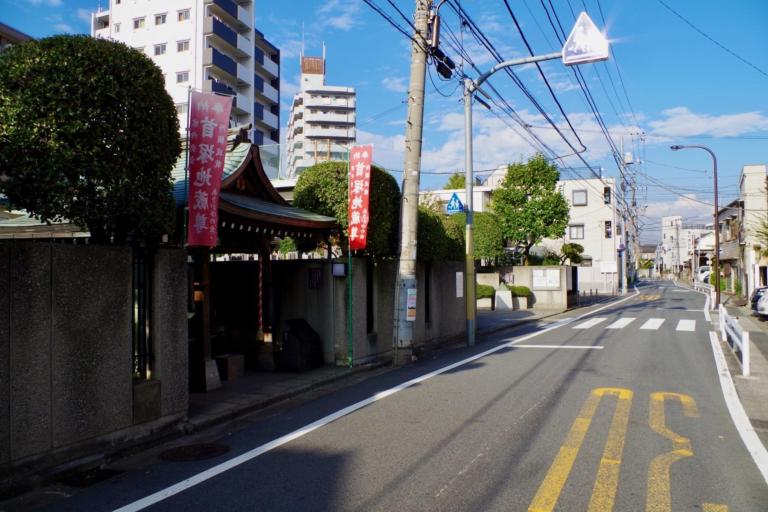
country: JP
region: Saitama
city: Soka
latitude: 35.7325
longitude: 139.8167
